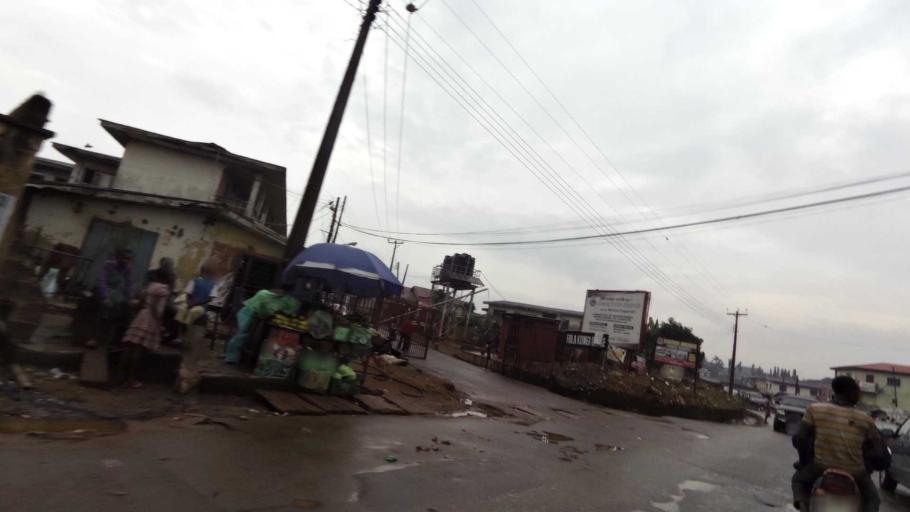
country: NG
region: Oyo
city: Ibadan
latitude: 7.4150
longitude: 3.9334
